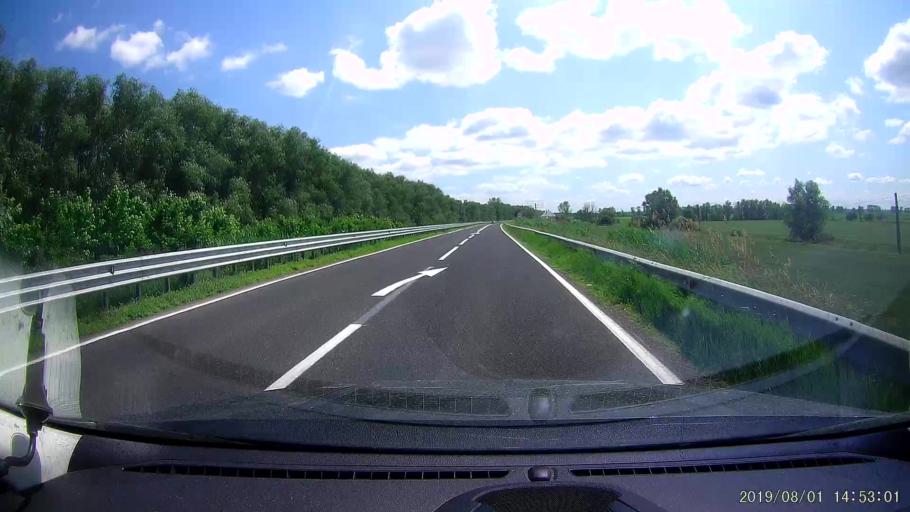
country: RO
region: Braila
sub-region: Comuna Vadeni
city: Vadeni
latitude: 45.3443
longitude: 28.0074
